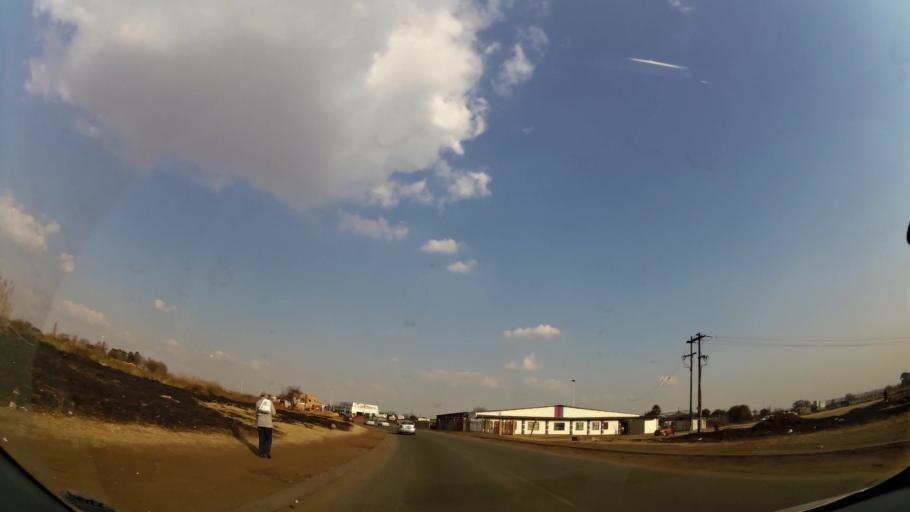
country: ZA
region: Gauteng
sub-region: Ekurhuleni Metropolitan Municipality
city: Germiston
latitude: -26.3455
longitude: 28.1863
